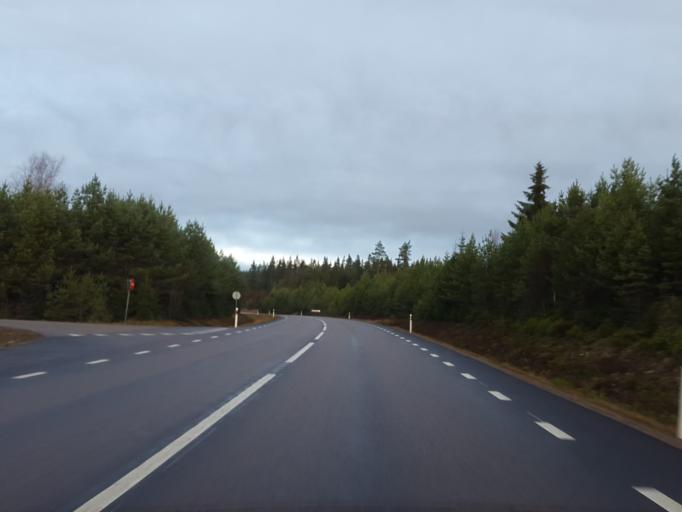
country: SE
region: Vaestra Goetaland
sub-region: Boras Kommun
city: Sandared
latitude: 57.7922
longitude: 12.7695
